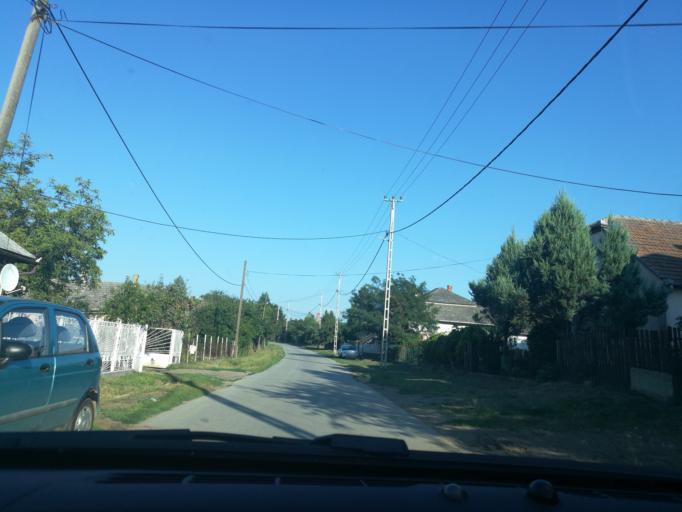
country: HU
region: Szabolcs-Szatmar-Bereg
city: Tiszabercel
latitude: 48.1685
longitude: 21.5810
